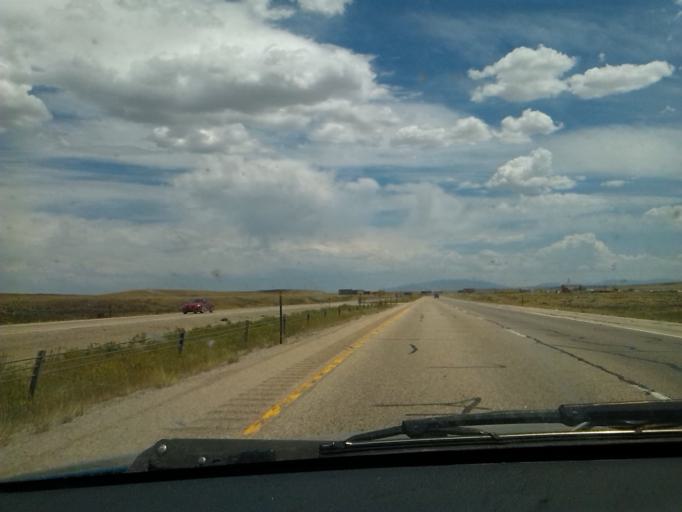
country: US
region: Wyoming
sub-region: Carbon County
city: Rawlins
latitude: 41.7864
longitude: -107.1827
